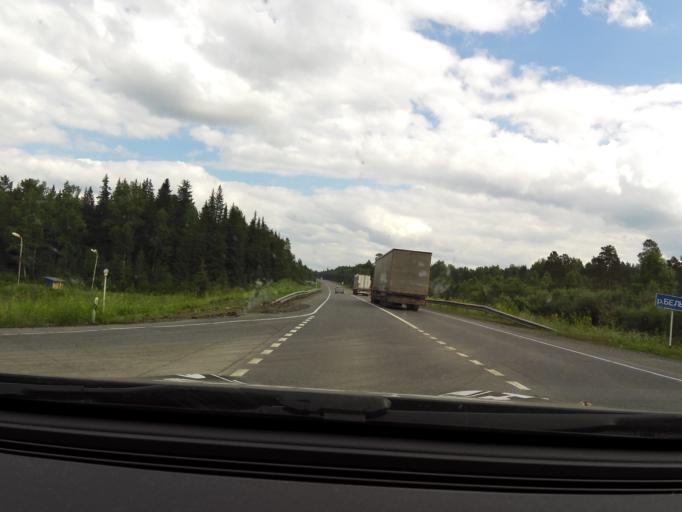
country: RU
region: Sverdlovsk
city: Atig
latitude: 56.8043
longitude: 59.3751
